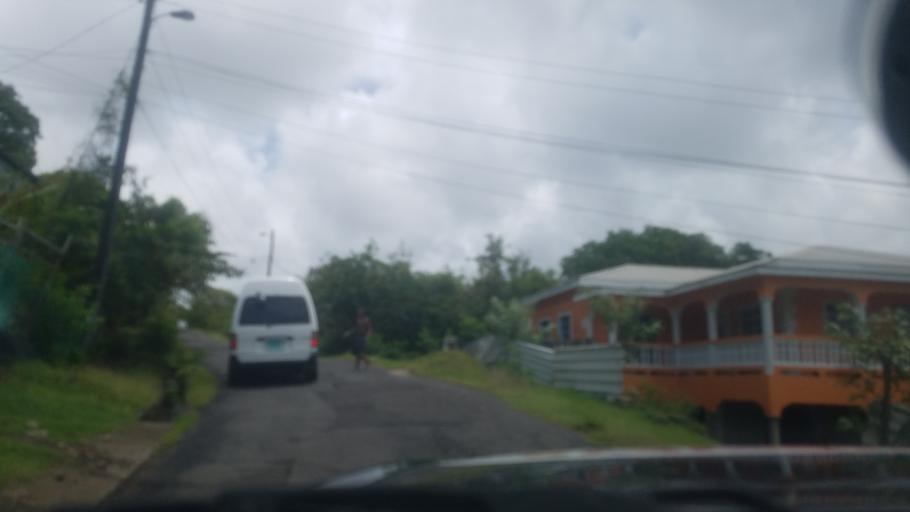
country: LC
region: Laborie Quarter
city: Laborie
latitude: 13.7432
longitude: -60.9627
